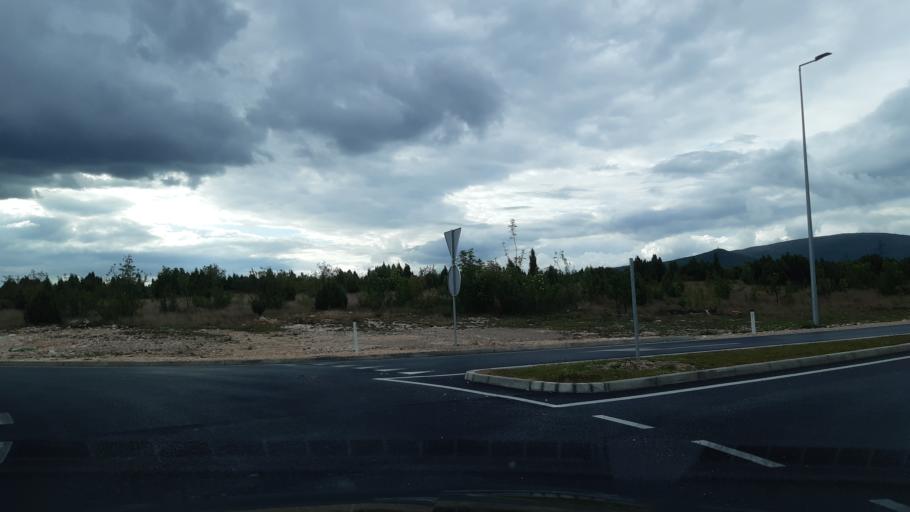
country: BA
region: Federation of Bosnia and Herzegovina
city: Rodoc
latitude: 43.3114
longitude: 17.7734
